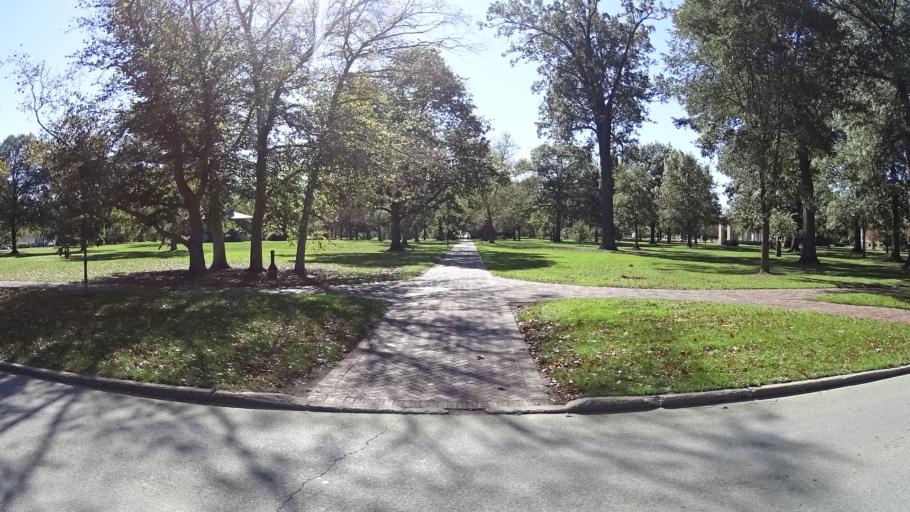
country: US
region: Ohio
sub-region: Lorain County
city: Oberlin
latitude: 41.2942
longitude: -82.2186
